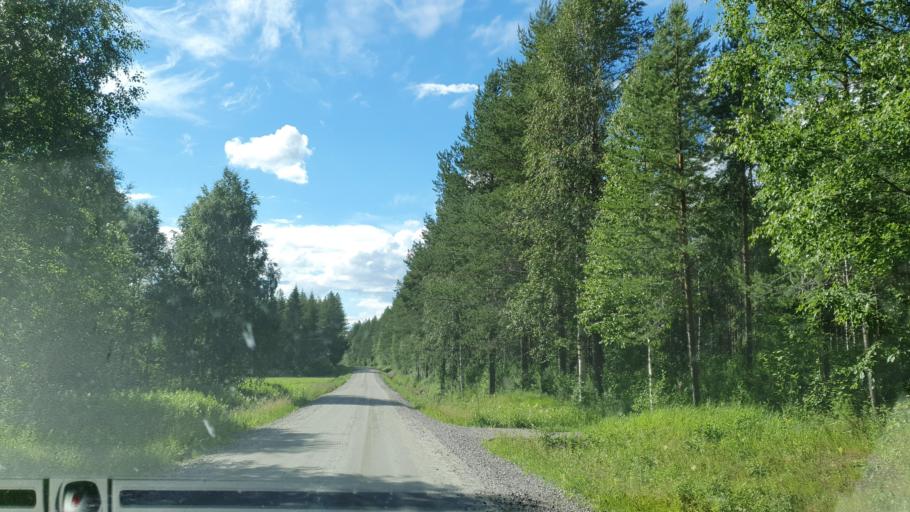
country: FI
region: Kainuu
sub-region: Kehys-Kainuu
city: Kuhmo
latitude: 64.1464
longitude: 29.7678
